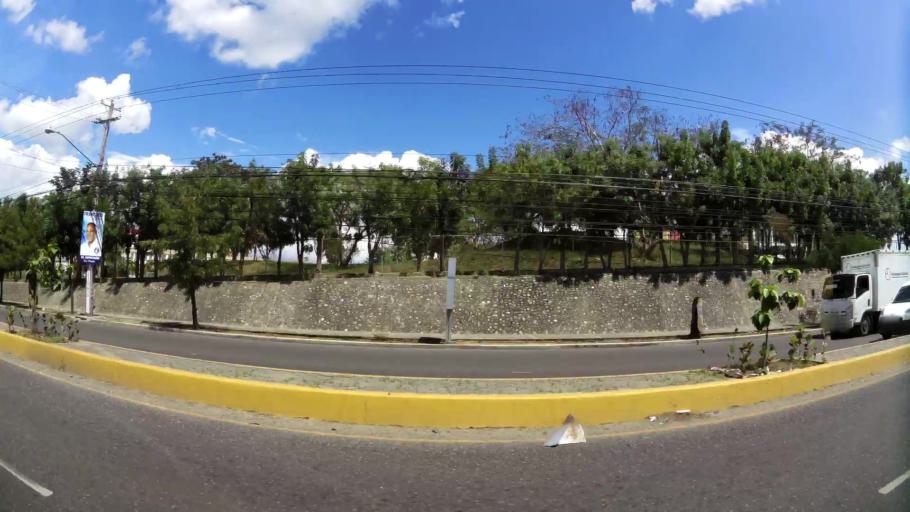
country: DO
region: Santiago
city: Santiago de los Caballeros
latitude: 19.4435
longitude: -70.6872
